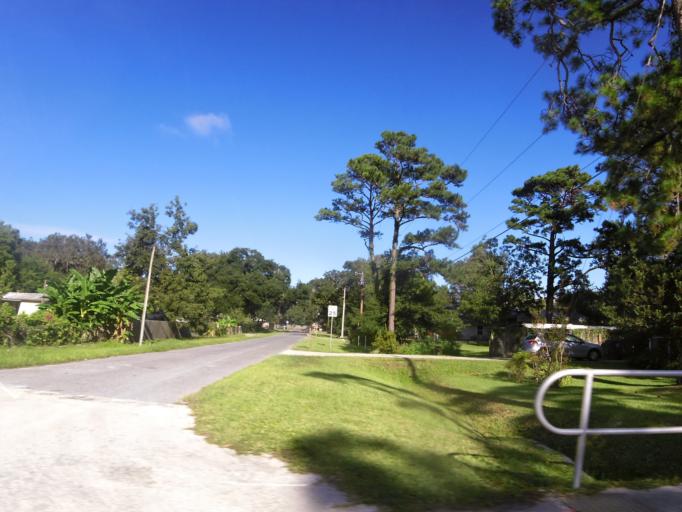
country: US
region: Florida
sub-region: Nassau County
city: Fernandina Beach
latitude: 30.6359
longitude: -81.4556
